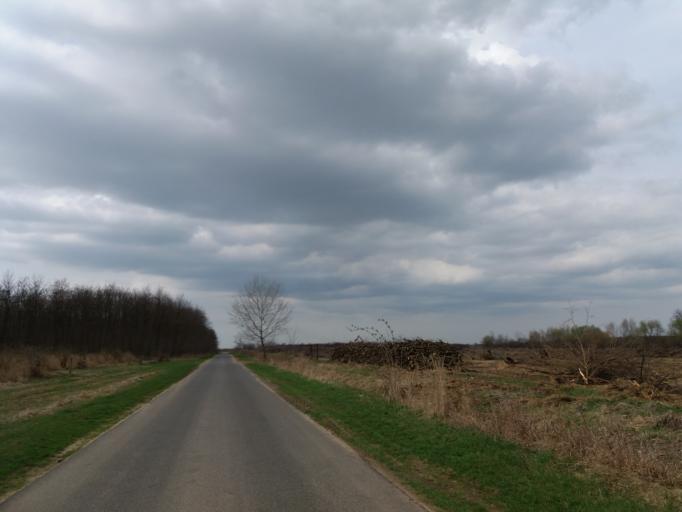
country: HU
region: Szabolcs-Szatmar-Bereg
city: Nyirtass
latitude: 48.0882
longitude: 22.0352
